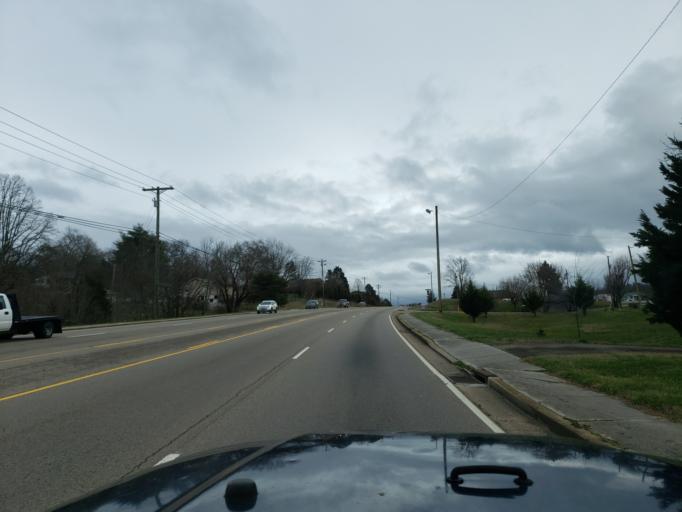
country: US
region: Tennessee
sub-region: Jefferson County
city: Jefferson City
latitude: 36.1056
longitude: -83.4844
